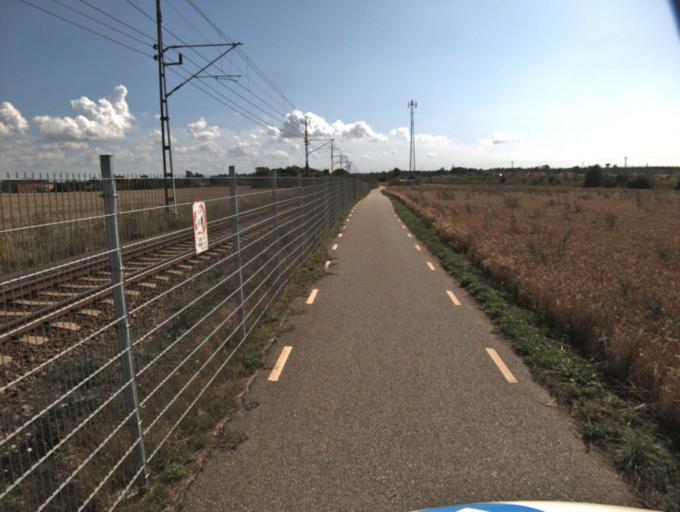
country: SE
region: Skane
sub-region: Kavlinge Kommun
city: Kaevlinge
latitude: 55.8110
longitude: 13.1096
